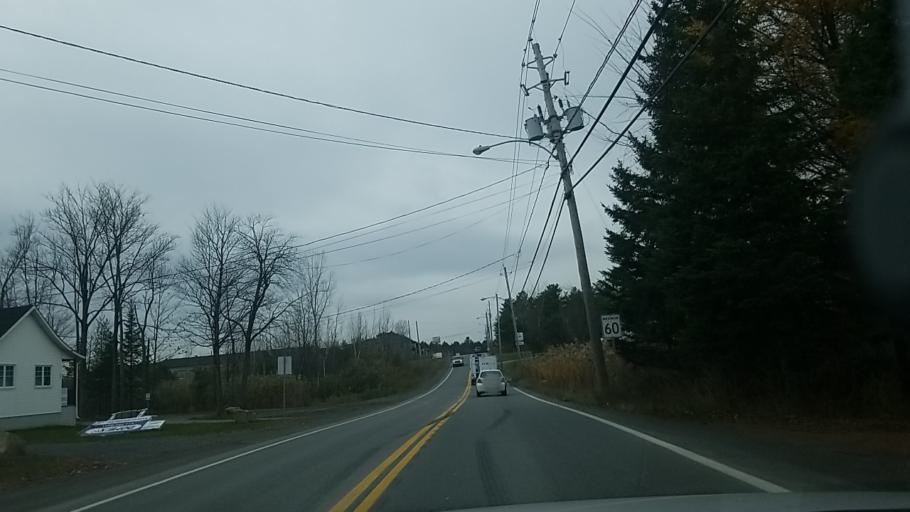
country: CA
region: Quebec
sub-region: Laurentides
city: Saint-Jerome
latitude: 45.7769
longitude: -74.0424
